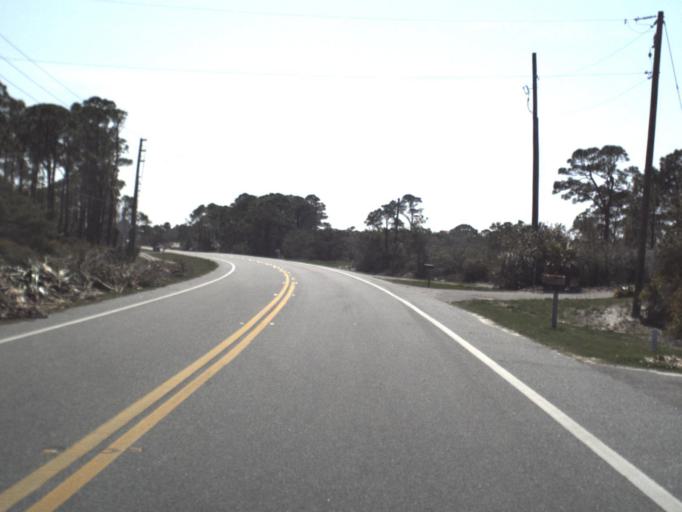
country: US
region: Florida
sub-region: Gulf County
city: Port Saint Joe
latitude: 29.7435
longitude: -85.3956
